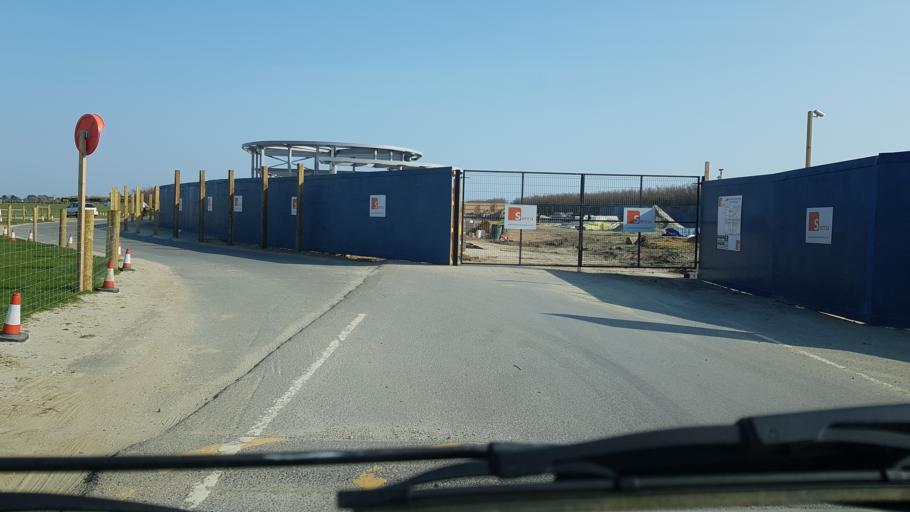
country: GB
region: England
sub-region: West Sussex
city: East Wittering
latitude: 50.7770
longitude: -0.9094
